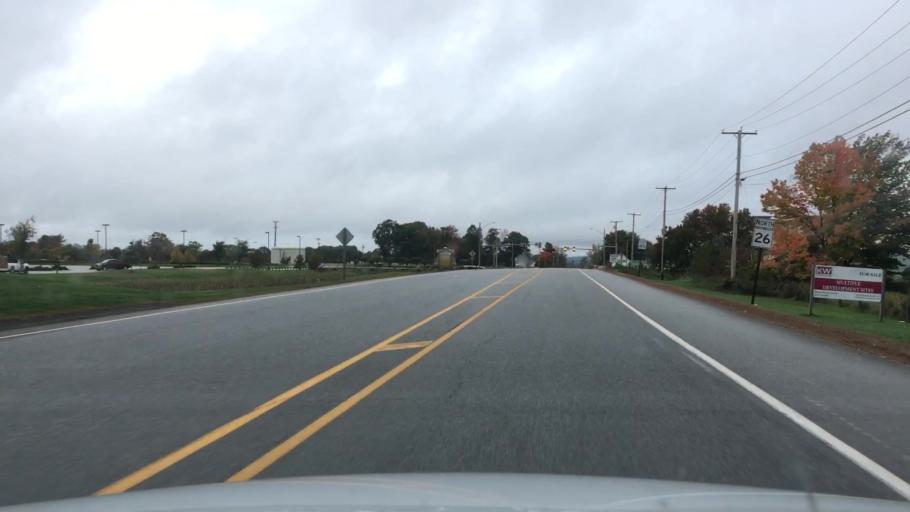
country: US
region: Maine
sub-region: Androscoggin County
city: Mechanic Falls
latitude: 44.1146
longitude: -70.4422
